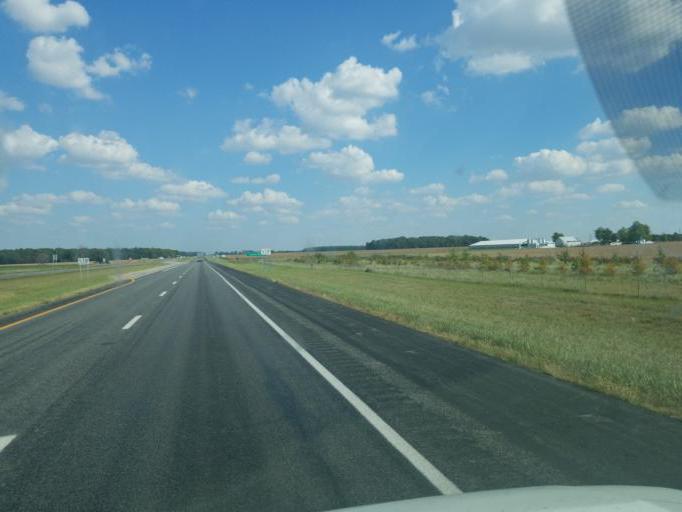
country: US
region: Ohio
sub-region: Hardin County
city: Ada
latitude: 40.8262
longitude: -83.7889
